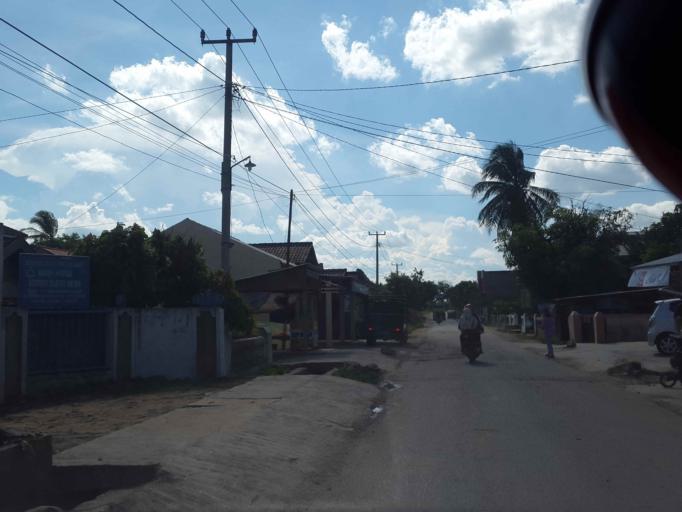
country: ID
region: Lampung
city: Natar
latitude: -5.2967
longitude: 105.1912
